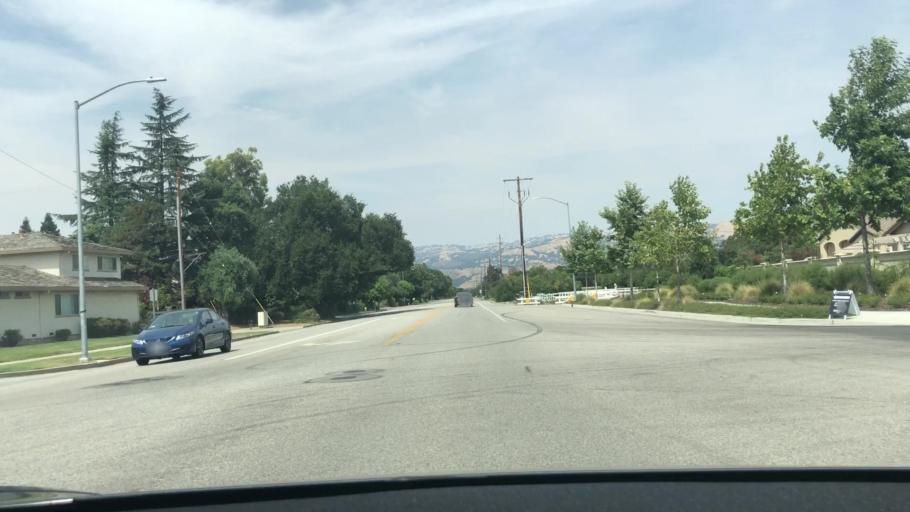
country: US
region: California
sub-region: Santa Clara County
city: Morgan Hill
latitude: 37.0995
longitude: -121.6421
